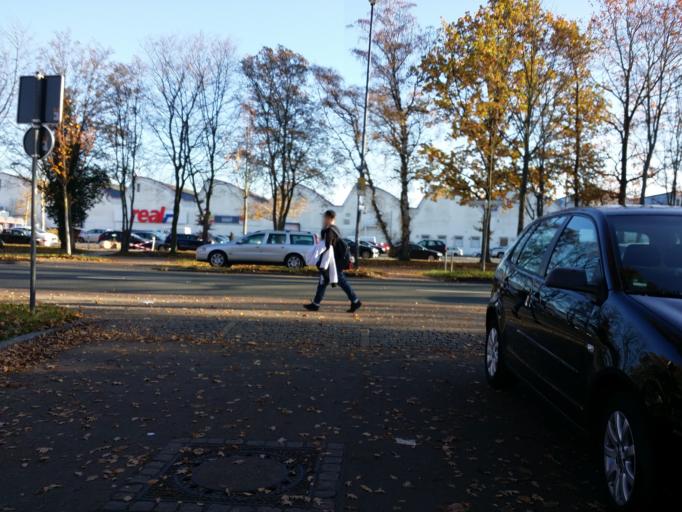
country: DE
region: Lower Saxony
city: Lilienthal
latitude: 53.0693
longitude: 8.8875
